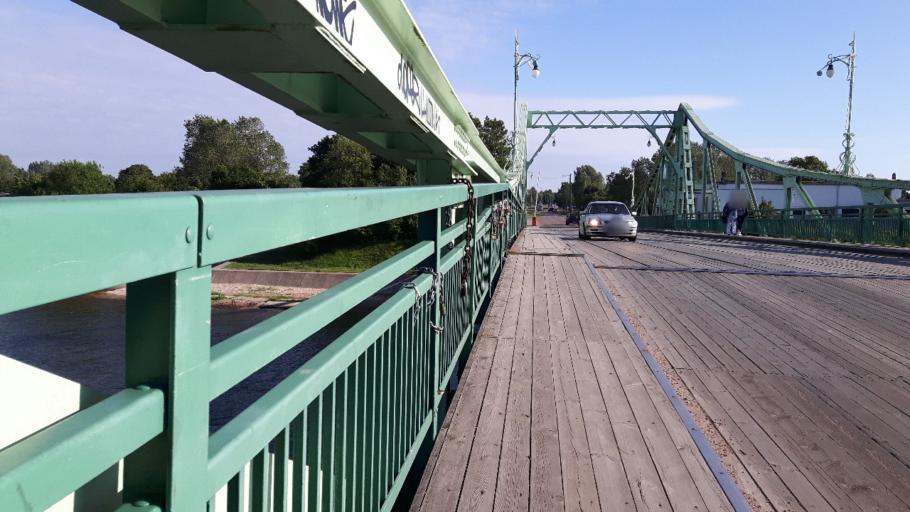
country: LV
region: Liepaja
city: Vec-Liepaja
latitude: 56.5454
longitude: 21.0047
